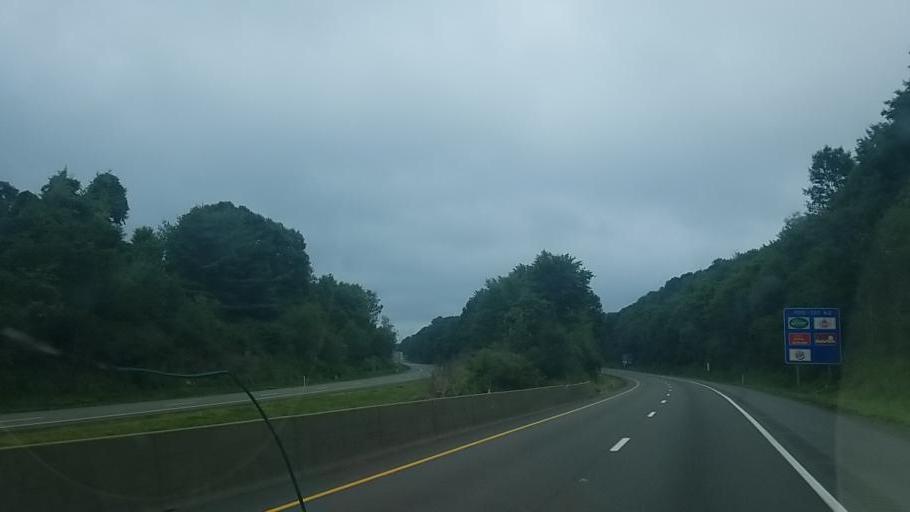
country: US
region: Pennsylvania
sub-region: Clarion County
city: Clarion
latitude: 41.1866
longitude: -79.4102
